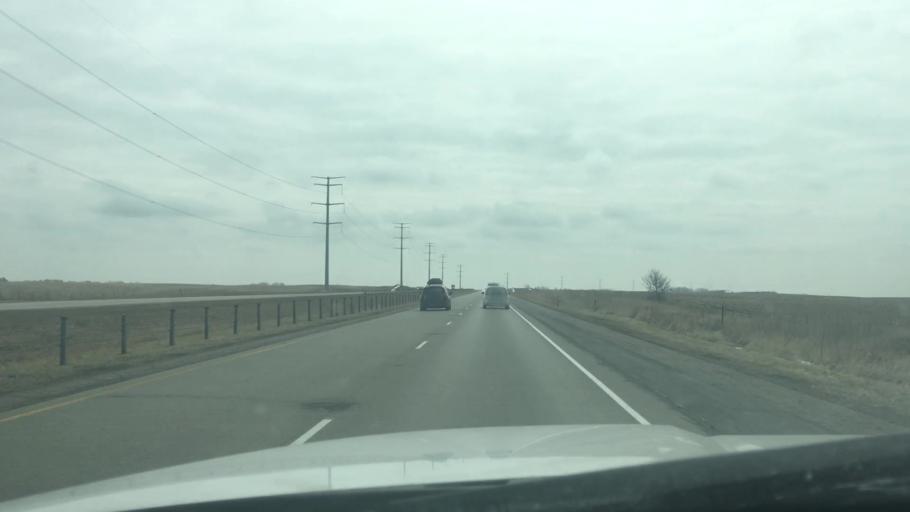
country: US
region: Minnesota
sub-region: Clay County
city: Barnesville
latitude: 46.5361
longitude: -96.3006
